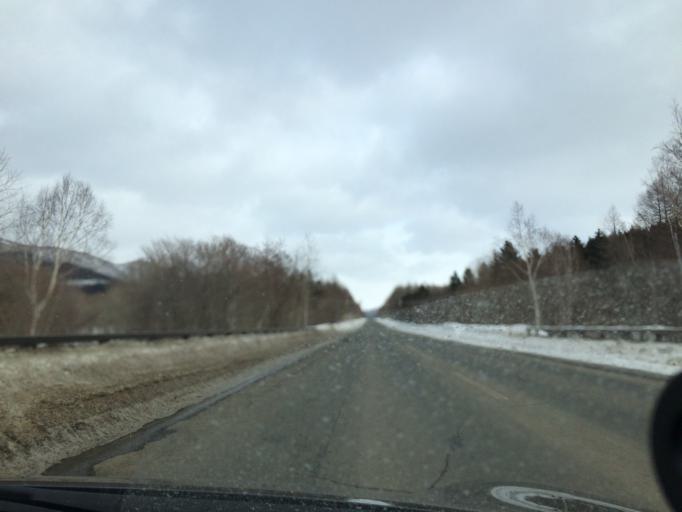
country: JP
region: Hokkaido
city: Shimo-furano
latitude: 43.1310
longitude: 142.6897
